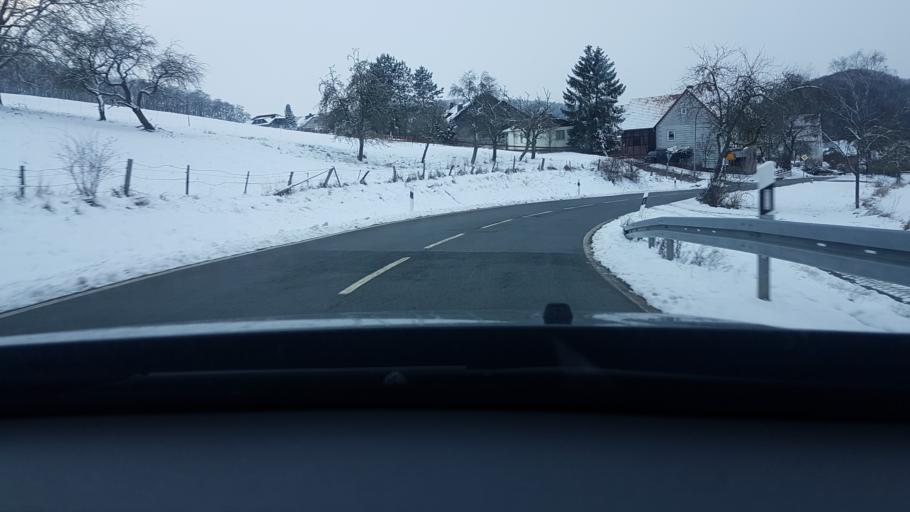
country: DE
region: Hesse
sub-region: Regierungsbezirk Kassel
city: Korbach
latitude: 51.3451
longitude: 8.8291
